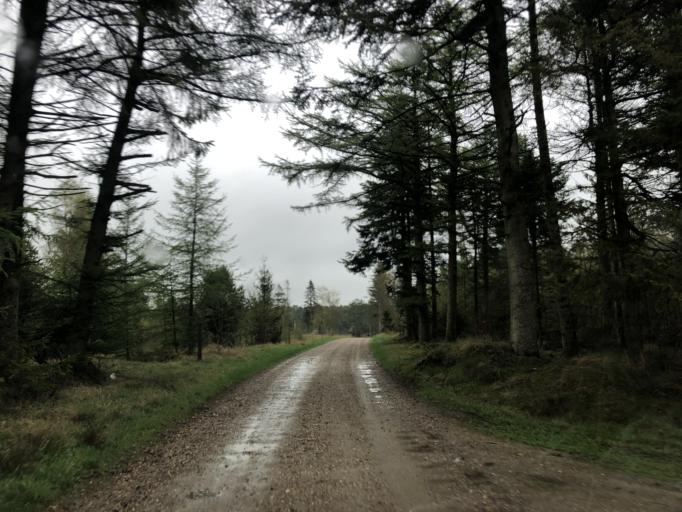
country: DK
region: Central Jutland
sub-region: Lemvig Kommune
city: Lemvig
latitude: 56.4496
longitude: 8.3900
